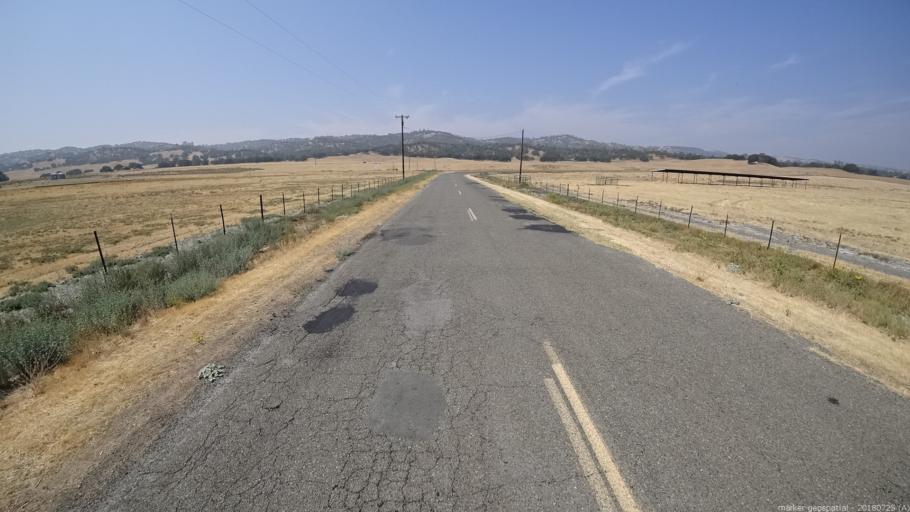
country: US
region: California
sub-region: San Luis Obispo County
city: Shandon
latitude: 35.8029
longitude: -120.3617
